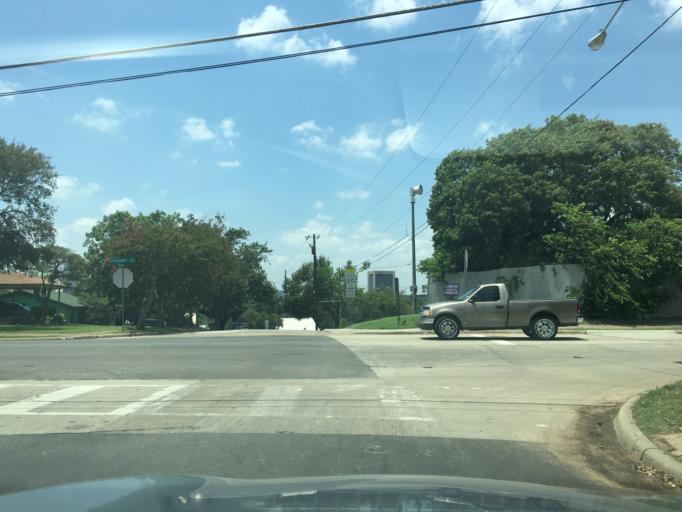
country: US
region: Texas
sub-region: Dallas County
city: Richardson
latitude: 32.9168
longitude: -96.7617
